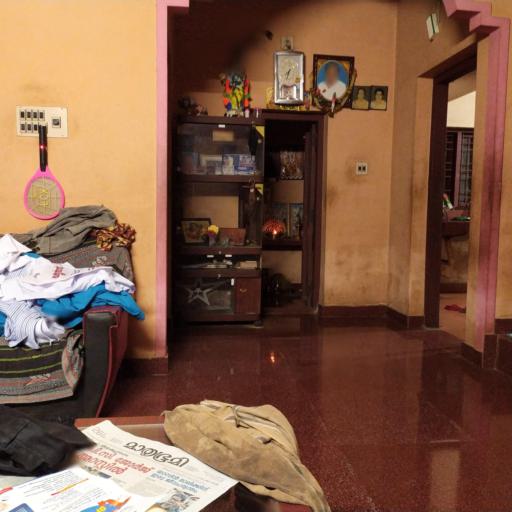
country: IN
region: Kerala
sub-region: Kasaragod District
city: Kannangad
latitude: 12.3243
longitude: 75.0906
